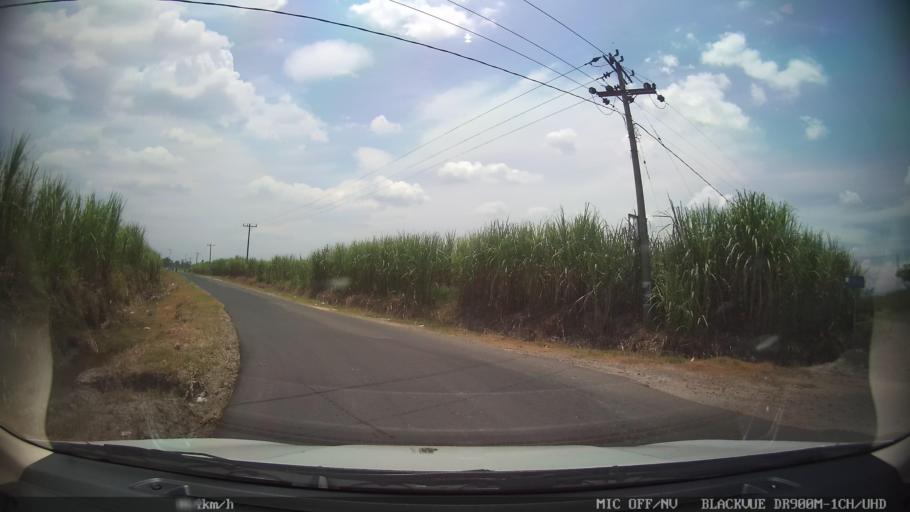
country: ID
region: North Sumatra
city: Binjai
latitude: 3.5902
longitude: 98.5412
